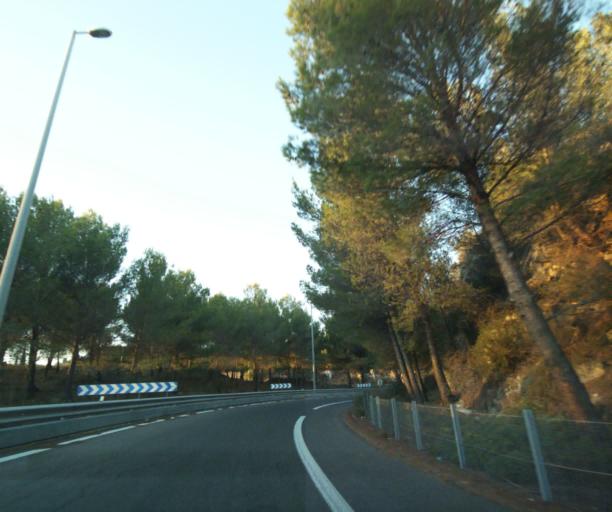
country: FR
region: Provence-Alpes-Cote d'Azur
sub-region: Departement des Bouches-du-Rhone
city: La Ciotat
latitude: 43.2042
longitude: 5.5940
